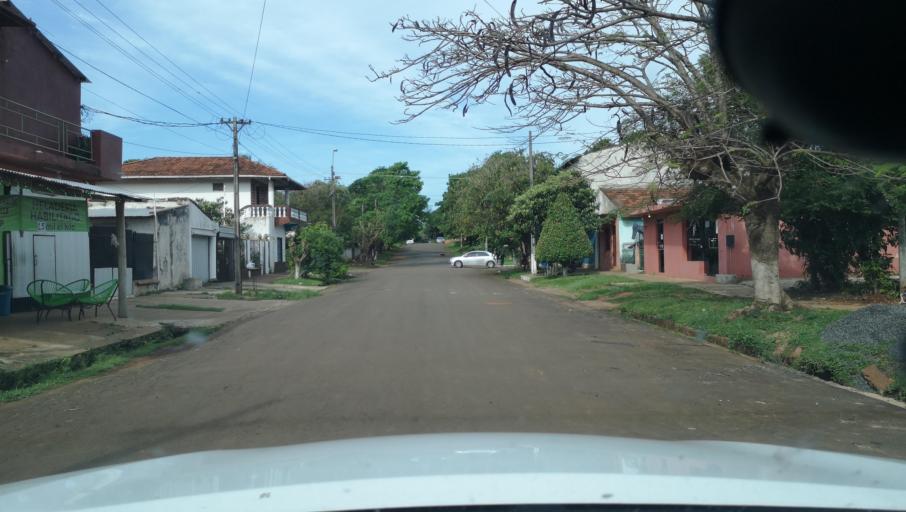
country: PY
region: Itapua
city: Carmen del Parana
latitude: -27.1623
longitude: -56.2382
